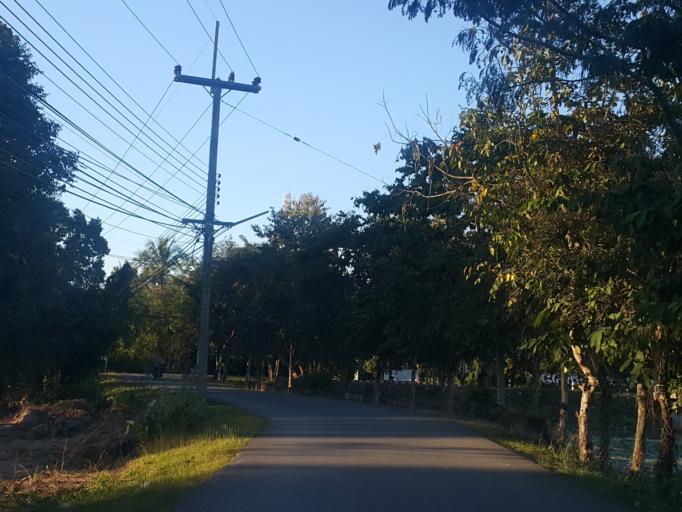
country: TH
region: Chiang Mai
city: San Sai
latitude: 18.8723
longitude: 99.1504
